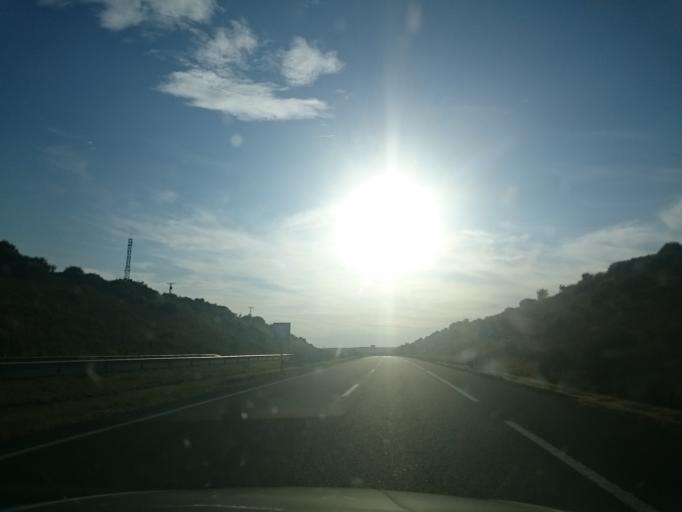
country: ES
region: Castille and Leon
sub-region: Provincia de Palencia
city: Ledigos
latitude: 42.3658
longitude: -4.8619
